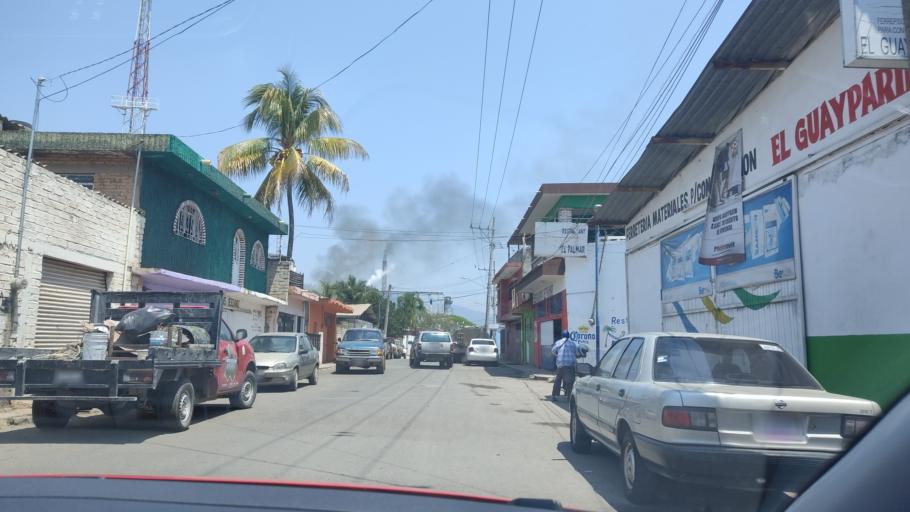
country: MX
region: Nayarit
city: Puga
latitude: 21.5810
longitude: -104.8249
